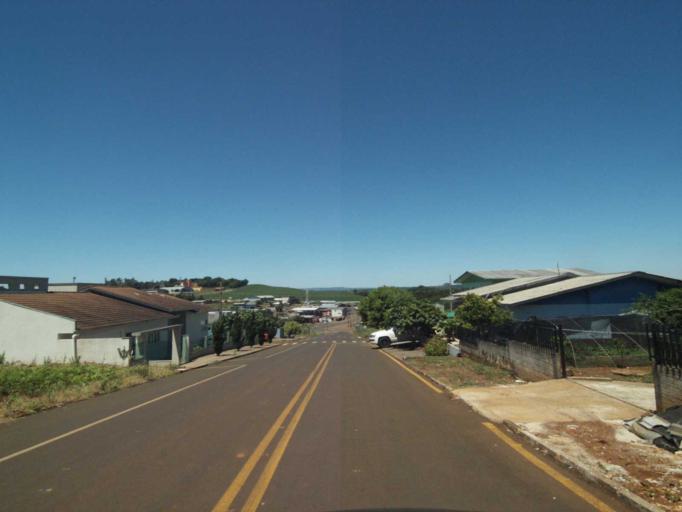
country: BR
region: Parana
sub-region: Coronel Vivida
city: Coronel Vivida
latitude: -25.9798
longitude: -52.8177
